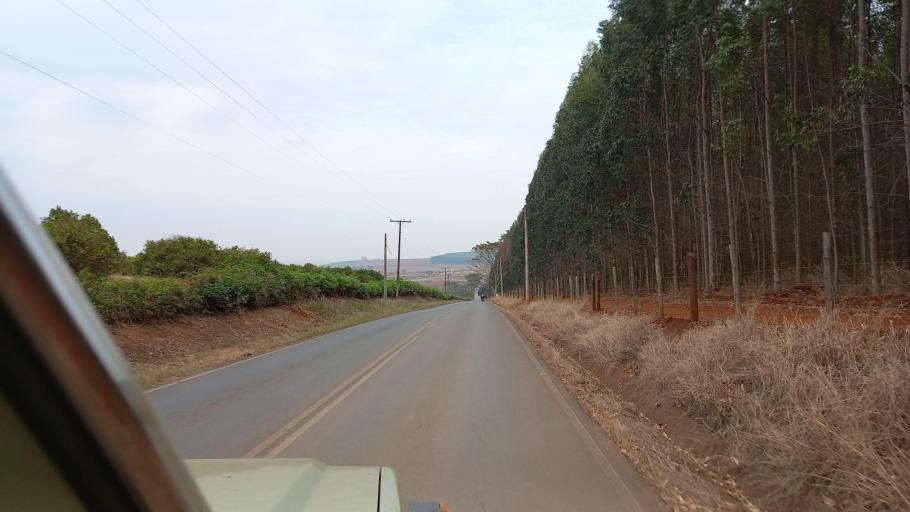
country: BR
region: Sao Paulo
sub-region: Moji-Guacu
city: Mogi-Gaucu
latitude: -22.3300
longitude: -46.8703
